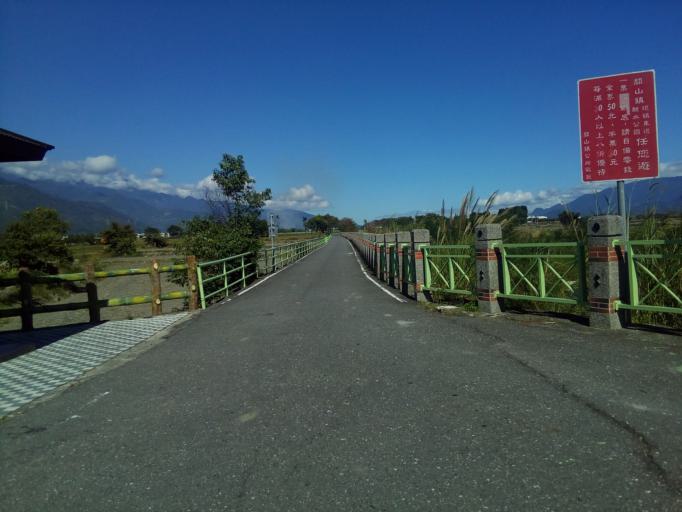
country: TW
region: Taiwan
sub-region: Taitung
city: Taitung
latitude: 23.0573
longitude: 121.1721
